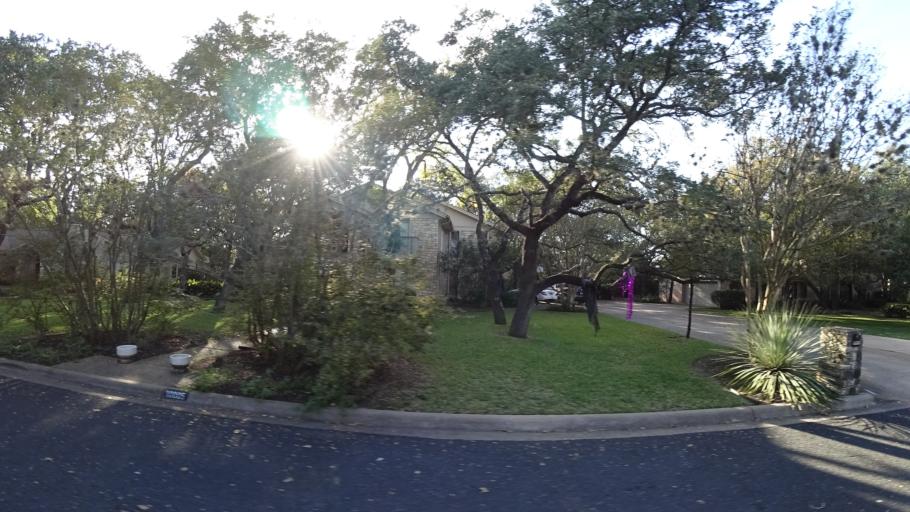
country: US
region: Texas
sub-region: Williamson County
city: Anderson Mill
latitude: 30.4363
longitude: -97.8056
